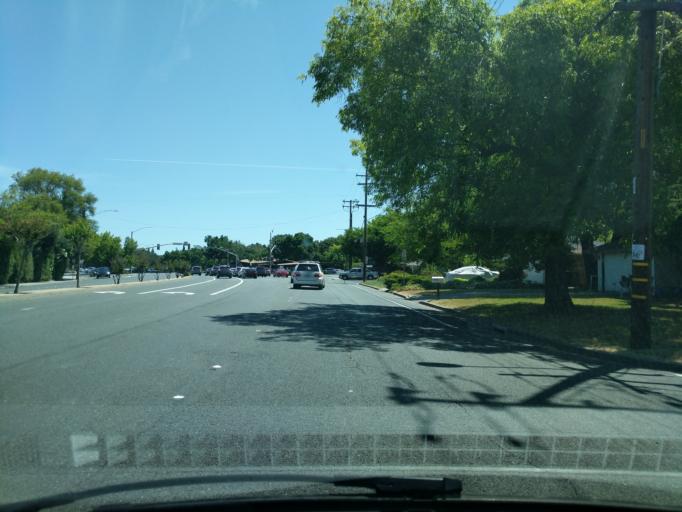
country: US
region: California
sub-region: Contra Costa County
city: Pleasant Hill
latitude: 37.9619
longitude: -122.0632
